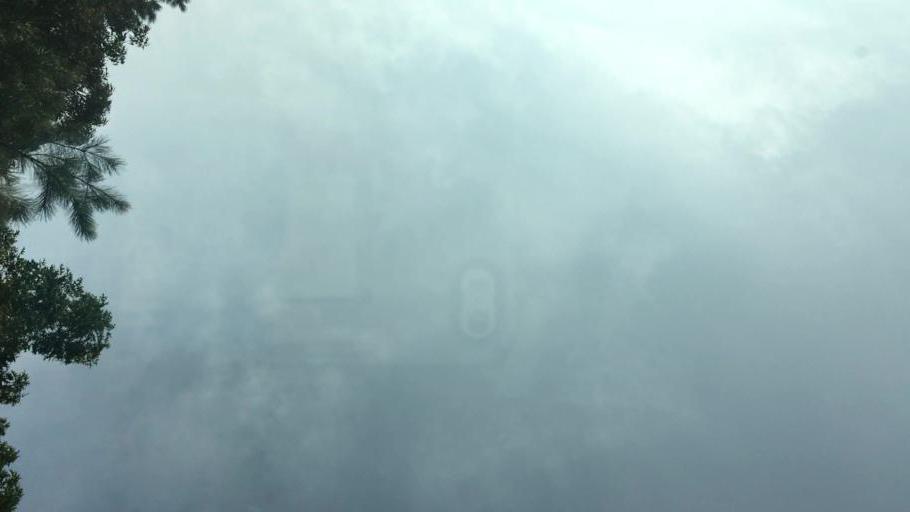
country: US
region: Alabama
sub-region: Bibb County
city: Woodstock
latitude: 33.2136
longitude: -87.0873
